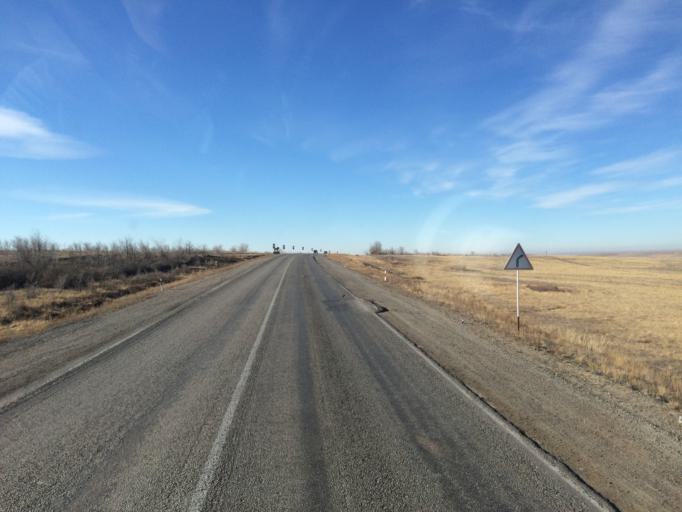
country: KZ
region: Aqtoebe
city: Aqtobe
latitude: 50.2821
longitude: 57.7532
